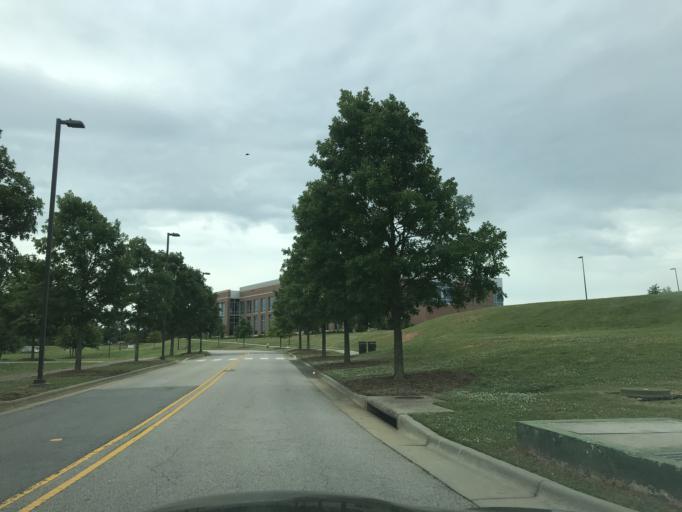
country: US
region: North Carolina
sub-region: Wake County
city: West Raleigh
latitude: 35.7968
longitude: -78.7051
